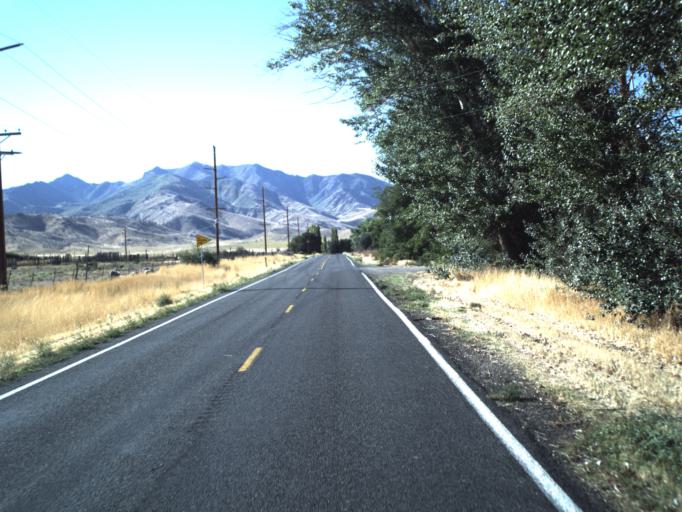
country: US
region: Utah
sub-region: Millard County
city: Delta
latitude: 39.4764
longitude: -112.2688
